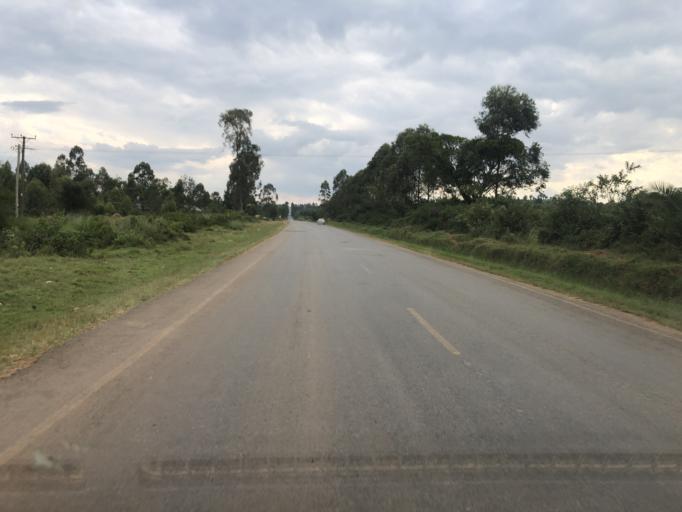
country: UG
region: Western Region
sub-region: Sheema District
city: Kibingo
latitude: -0.5793
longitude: 30.4233
